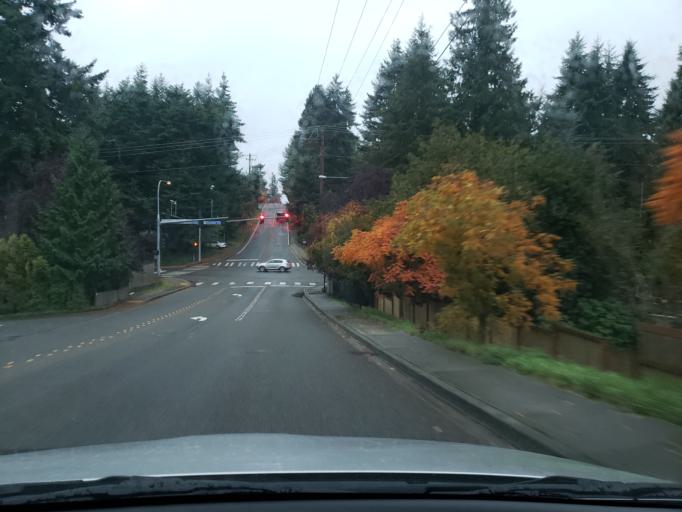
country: US
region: Washington
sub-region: Snohomish County
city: Meadowdale
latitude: 47.8393
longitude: -122.3239
